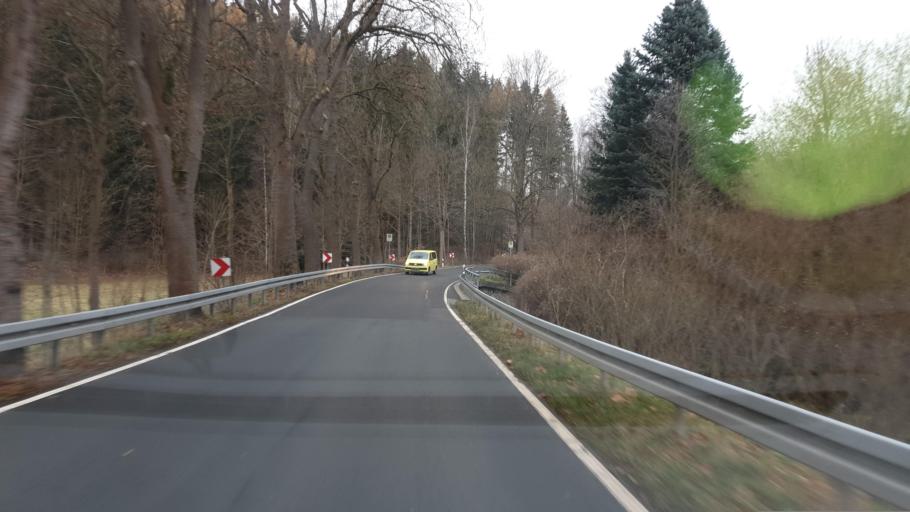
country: DE
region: Saxony
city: Mulda
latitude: 50.8004
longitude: 13.4061
